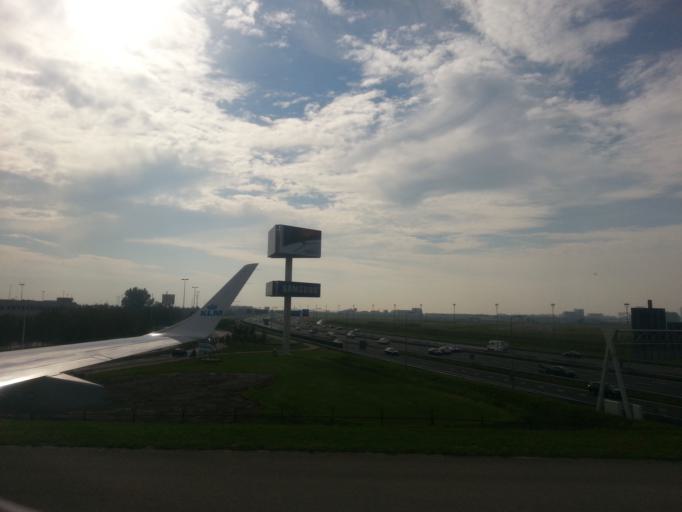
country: NL
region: North Holland
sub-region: Gemeente Aalsmeer
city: Aalsmeer
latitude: 52.3020
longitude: 4.7453
